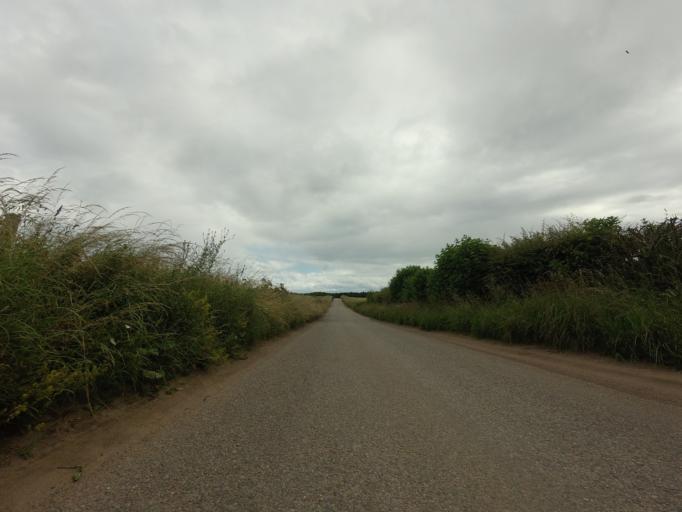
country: GB
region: Scotland
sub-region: Moray
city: Lhanbryd
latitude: 57.6612
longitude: -3.1874
